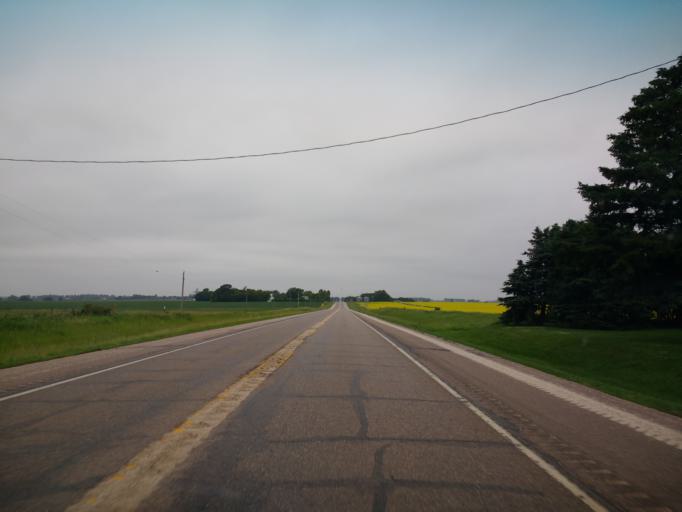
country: US
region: Iowa
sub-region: O'Brien County
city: Hartley
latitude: 43.1846
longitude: -95.4370
